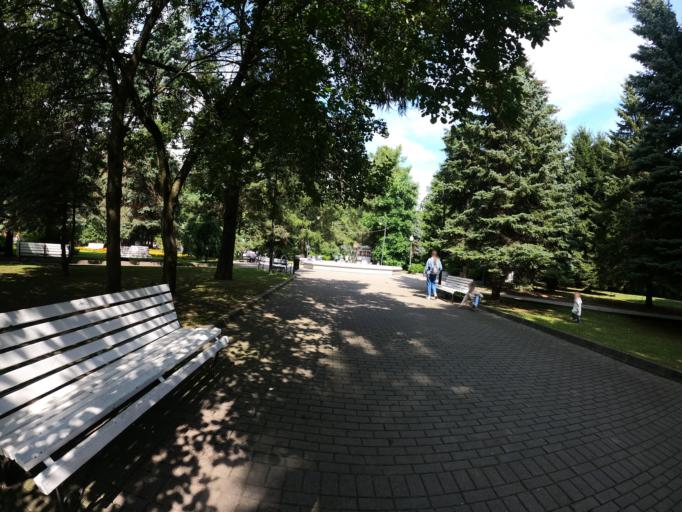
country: RU
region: Kaliningrad
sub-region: Gorod Kaliningrad
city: Kaliningrad
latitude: 54.7182
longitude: 20.4768
